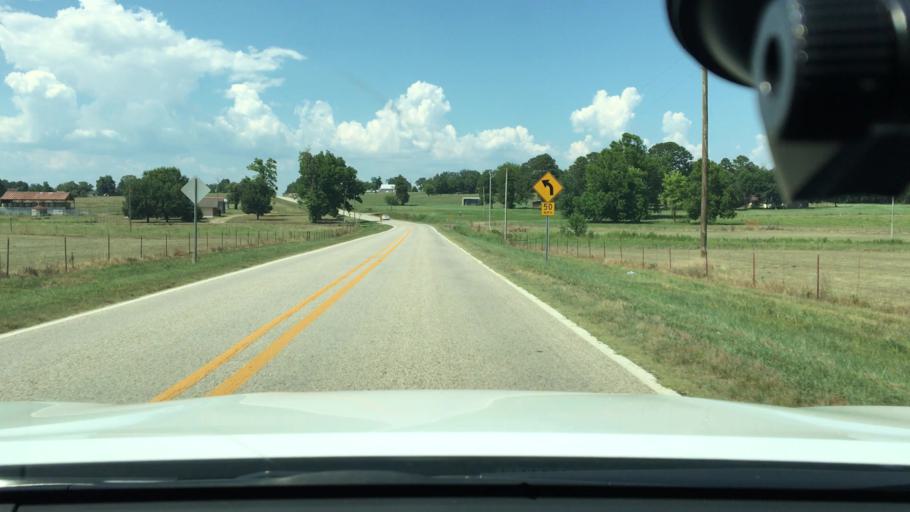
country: US
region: Arkansas
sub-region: Logan County
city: Paris
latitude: 35.3066
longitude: -93.6329
